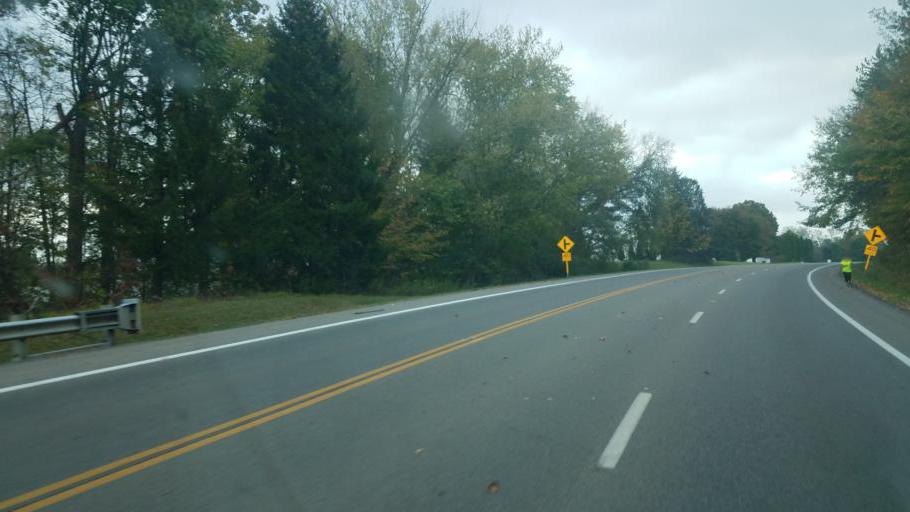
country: US
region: Ohio
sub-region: Holmes County
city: Millersburg
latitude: 40.5586
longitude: -81.8910
